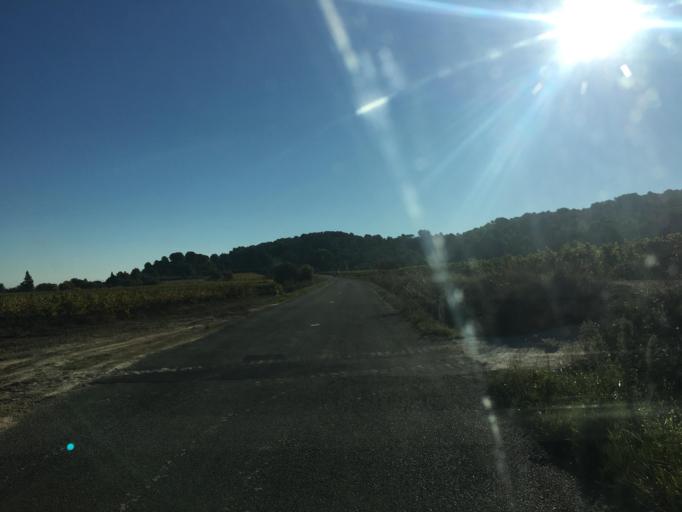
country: FR
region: Languedoc-Roussillon
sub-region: Departement de l'Aude
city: Fleury
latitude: 43.2352
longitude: 3.1558
